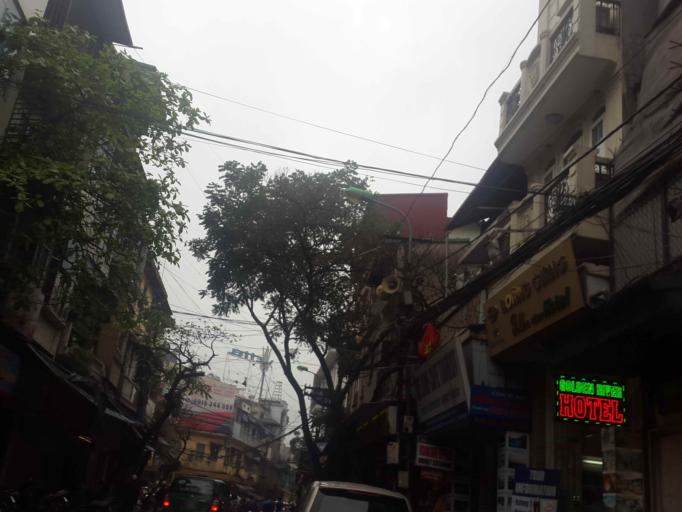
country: VN
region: Ha Noi
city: Hoan Kiem
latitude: 21.0329
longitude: 105.8503
